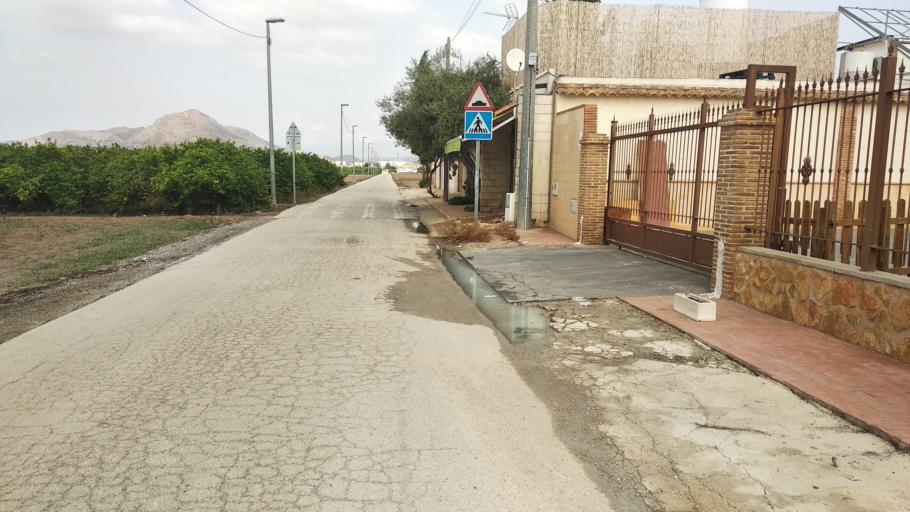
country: ES
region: Murcia
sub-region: Murcia
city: Santomera
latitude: 38.0378
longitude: -1.0386
